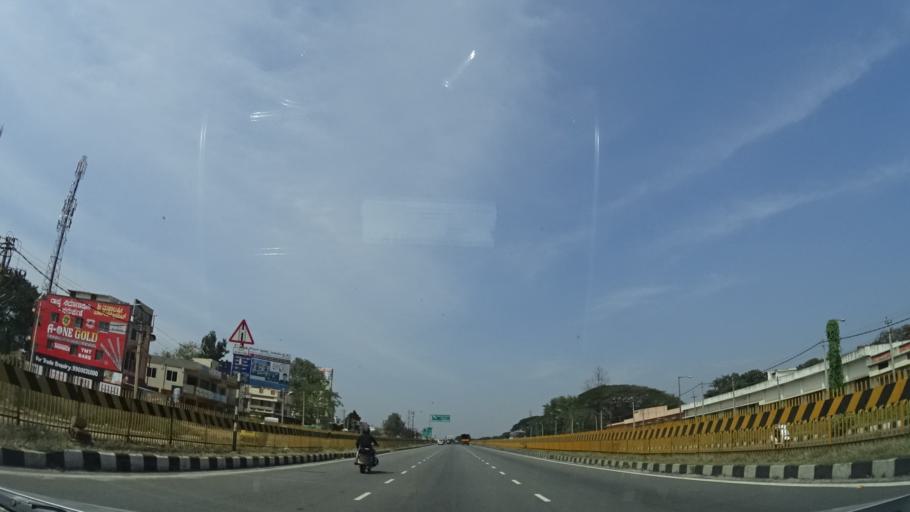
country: IN
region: Karnataka
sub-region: Tumkur
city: Tumkur
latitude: 13.3247
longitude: 77.1345
